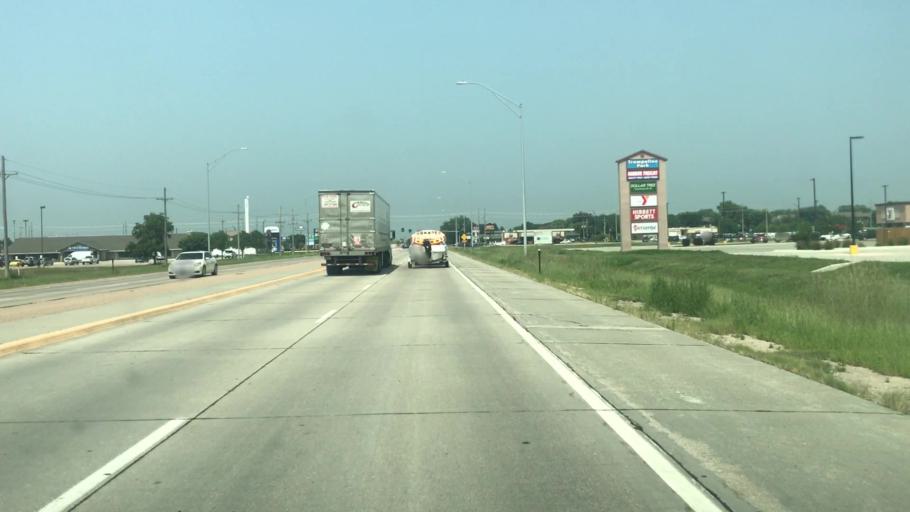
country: US
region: Nebraska
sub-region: Hall County
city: Grand Island
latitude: 40.9430
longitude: -98.3835
